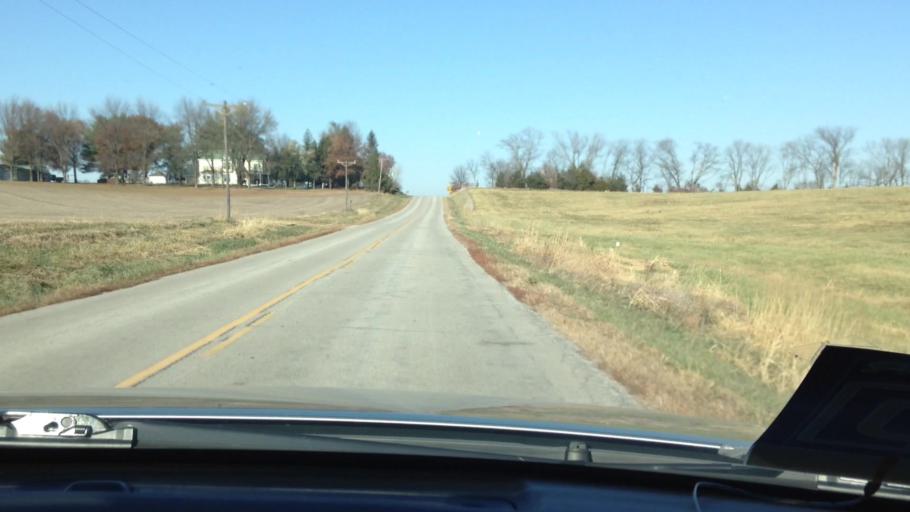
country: US
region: Missouri
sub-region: Platte County
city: Weston
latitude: 39.4405
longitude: -94.8544
